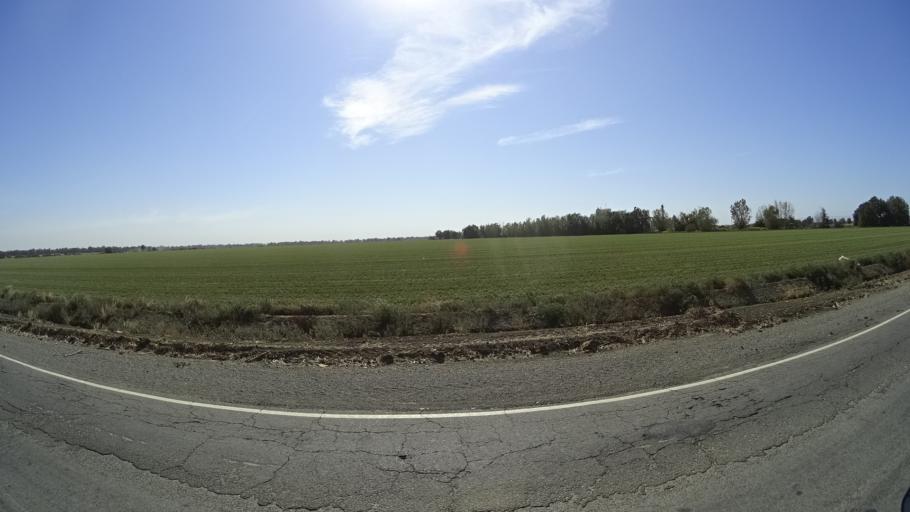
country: US
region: California
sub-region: Yolo County
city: Woodland
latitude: 38.6197
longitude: -121.7589
